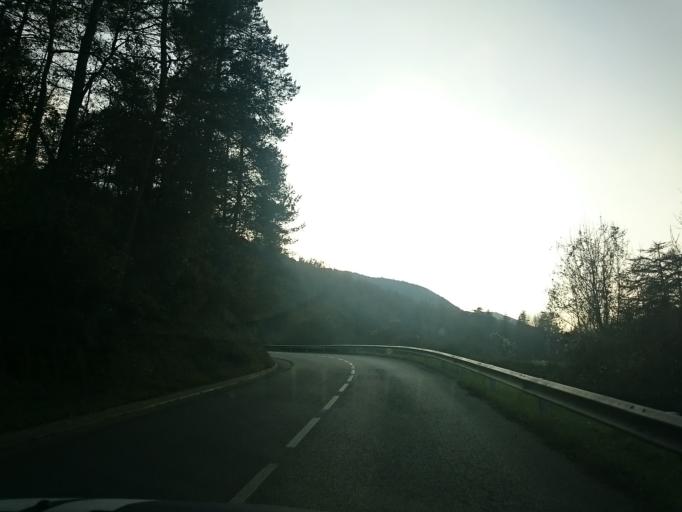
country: ES
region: Catalonia
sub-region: Provincia de Girona
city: Viladrau
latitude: 41.8549
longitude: 2.3501
